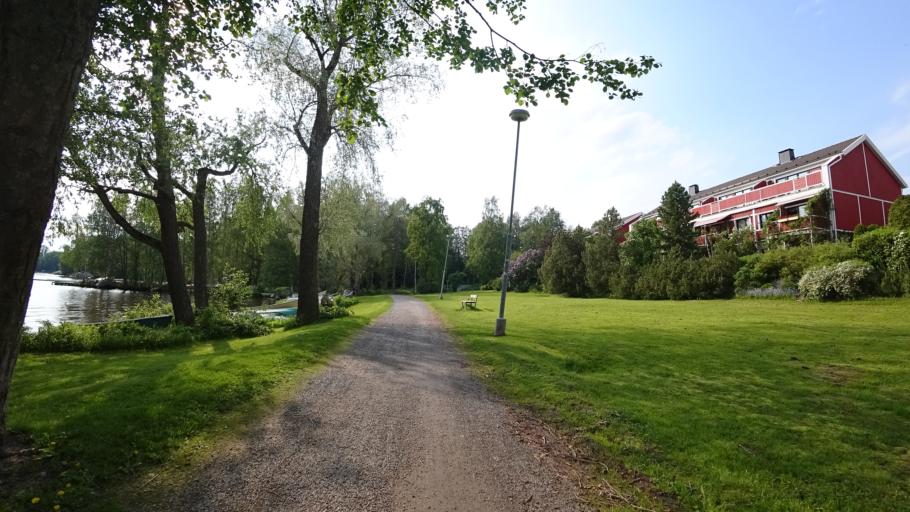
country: FI
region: Pirkanmaa
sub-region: Tampere
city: Pirkkala
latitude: 61.5036
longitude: 23.6987
